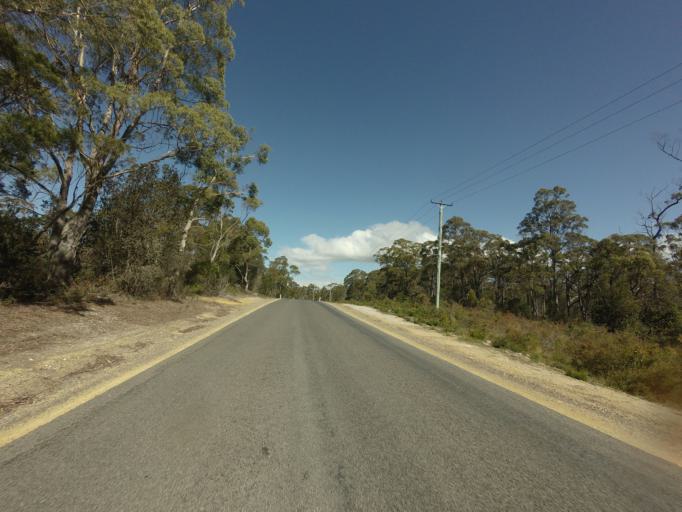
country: AU
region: Tasmania
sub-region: Break O'Day
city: St Helens
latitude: -41.6043
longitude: 148.2059
